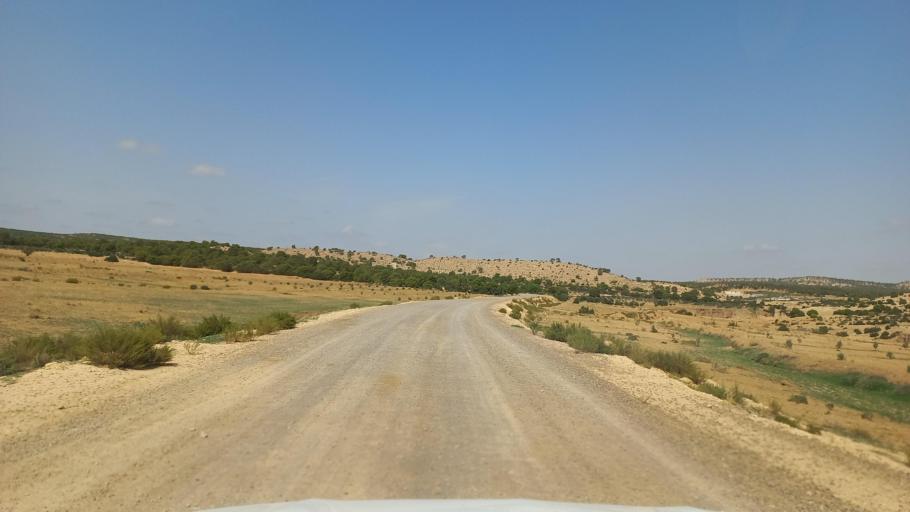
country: TN
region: Al Qasrayn
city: Sbiba
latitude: 35.3907
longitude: 8.9529
